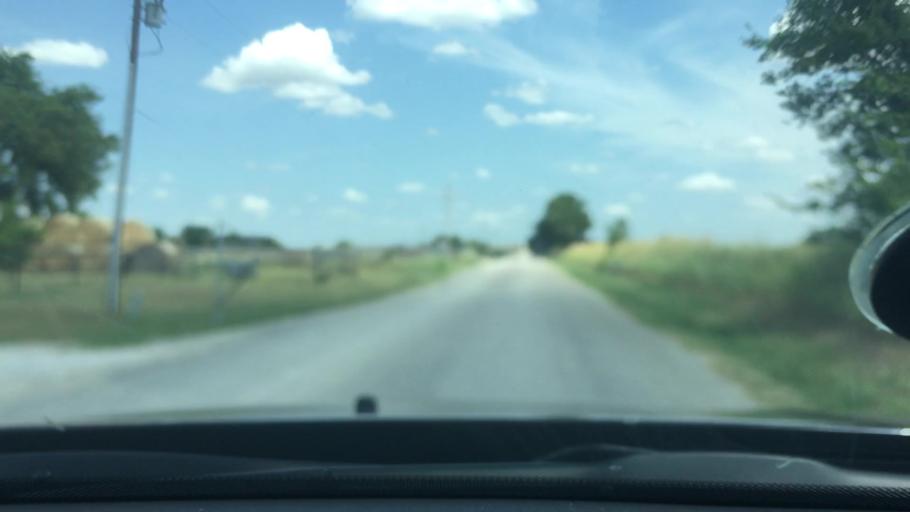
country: US
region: Oklahoma
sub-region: Love County
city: Marietta
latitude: 33.9478
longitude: -97.1869
